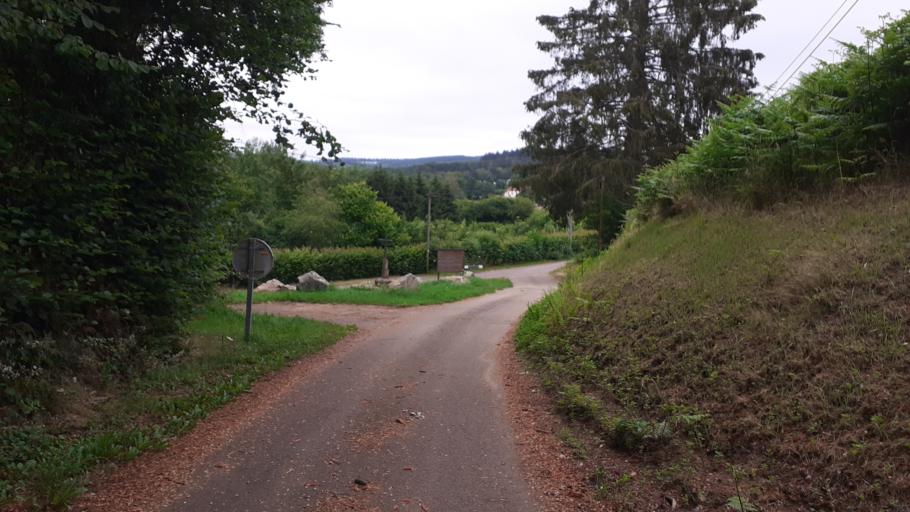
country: FR
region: Bourgogne
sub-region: Departement de la Cote-d'Or
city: Saulieu
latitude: 47.2717
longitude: 4.1394
